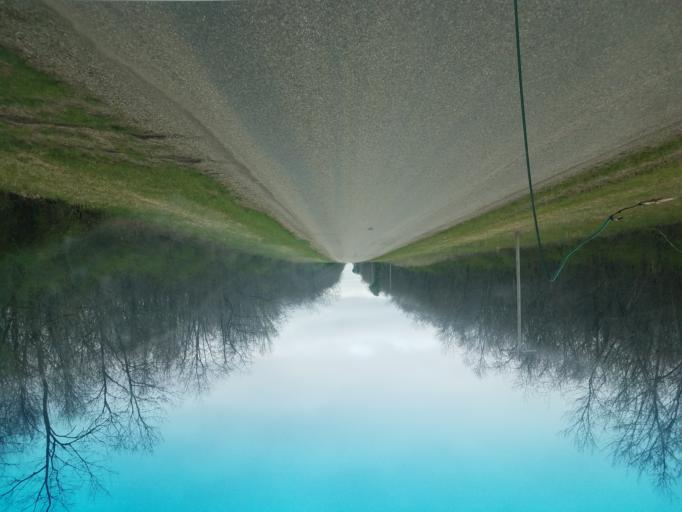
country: US
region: Ohio
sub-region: Stark County
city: Beach City
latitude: 40.6316
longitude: -81.6299
